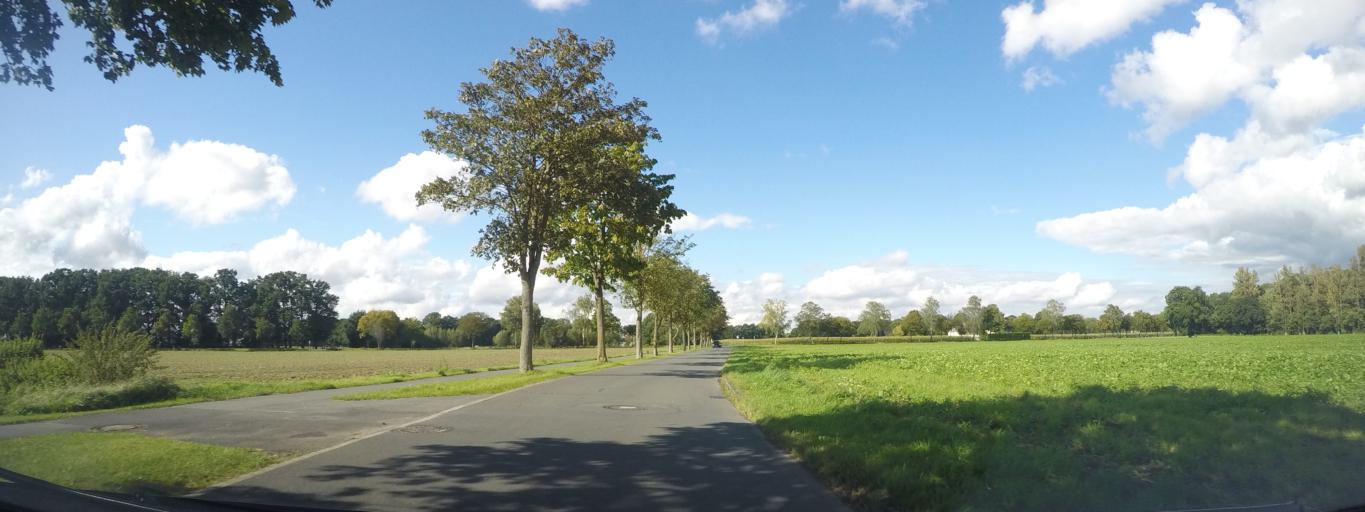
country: DE
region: North Rhine-Westphalia
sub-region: Regierungsbezirk Arnsberg
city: Lippstadt
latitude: 51.6933
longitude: 8.3107
